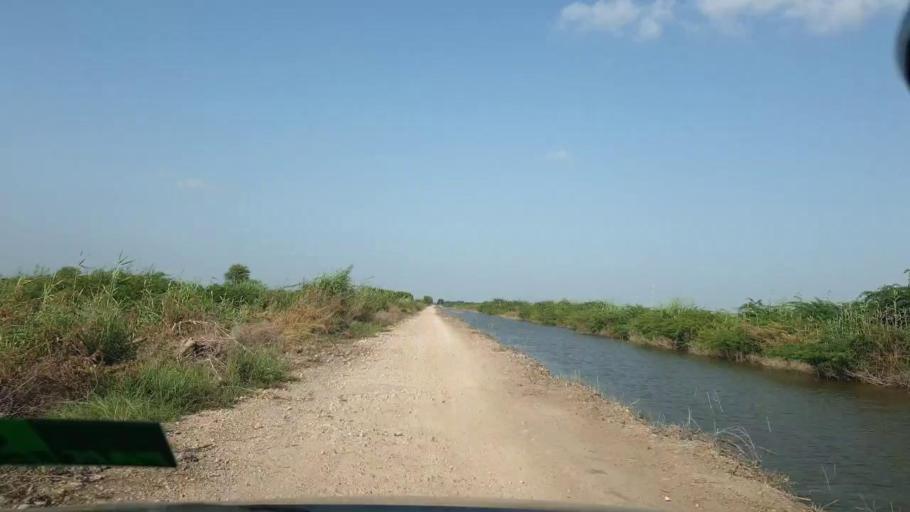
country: PK
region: Sindh
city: Tando Bago
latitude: 24.7037
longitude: 69.2011
